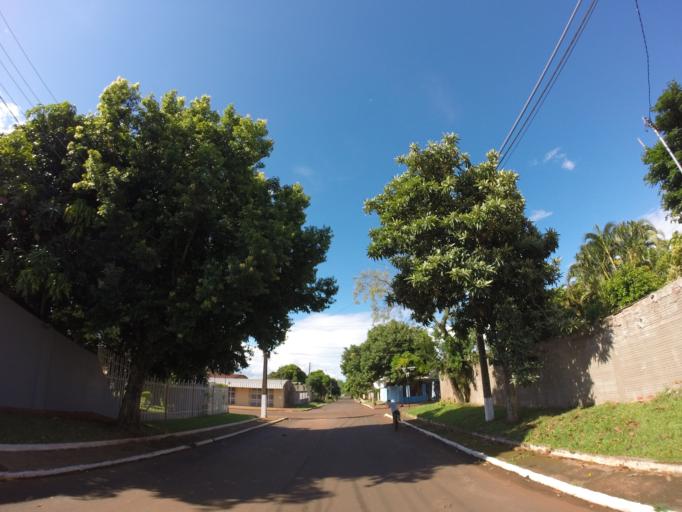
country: PY
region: Alto Parana
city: Ciudad del Este
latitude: -25.4029
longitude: -54.6243
